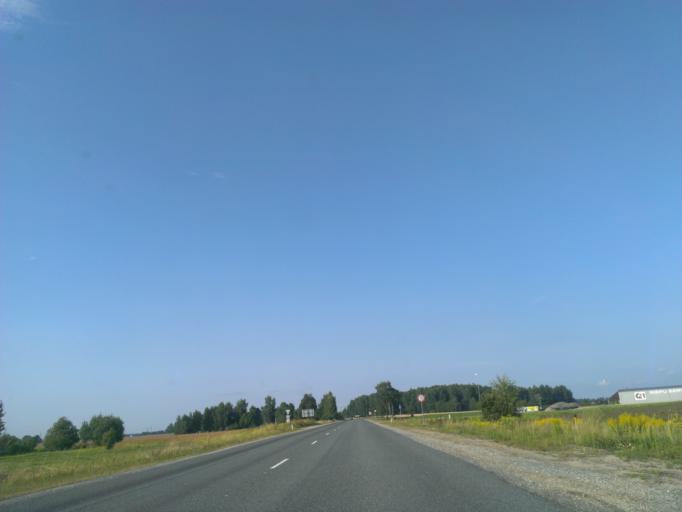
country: LV
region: Priekuli
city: Priekuli
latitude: 57.3141
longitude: 25.3197
